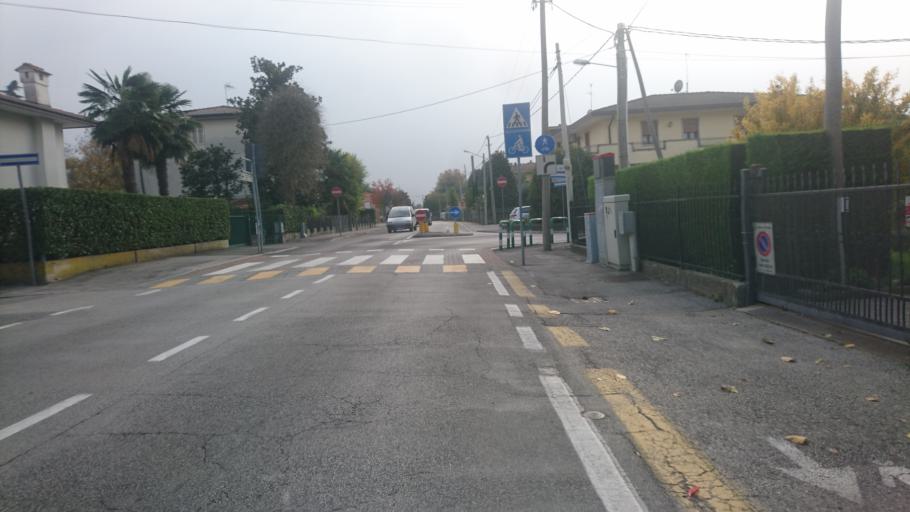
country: IT
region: Veneto
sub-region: Provincia di Padova
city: Cadoneghe
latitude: 45.4346
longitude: 11.9164
